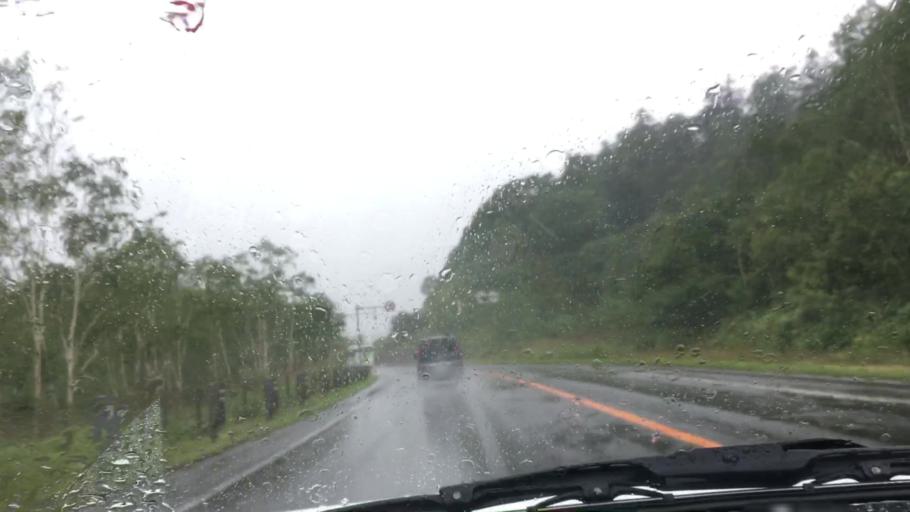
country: JP
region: Hokkaido
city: Sapporo
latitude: 42.8695
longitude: 141.1325
